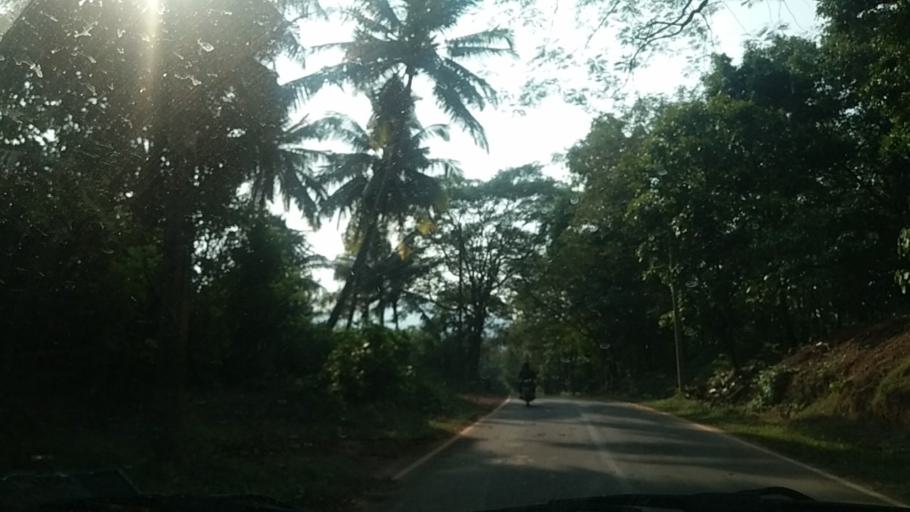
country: IN
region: Goa
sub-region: South Goa
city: Sanguem
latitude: 15.2153
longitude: 74.2043
